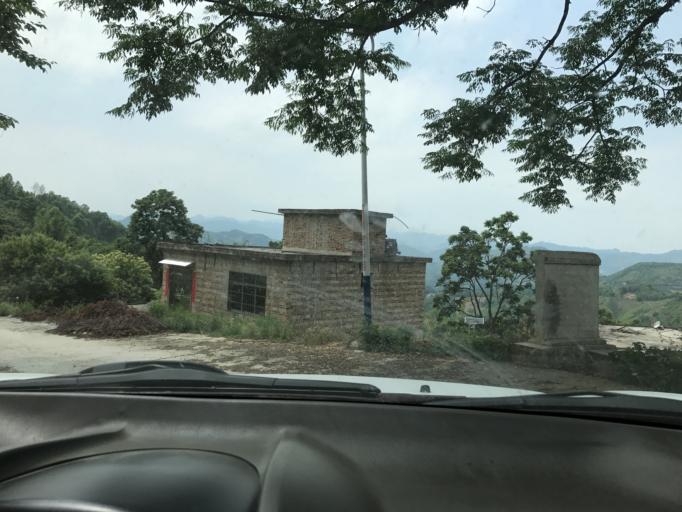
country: CN
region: Guangxi Zhuangzu Zizhiqu
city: Xinzhou
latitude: 24.9880
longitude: 105.9278
